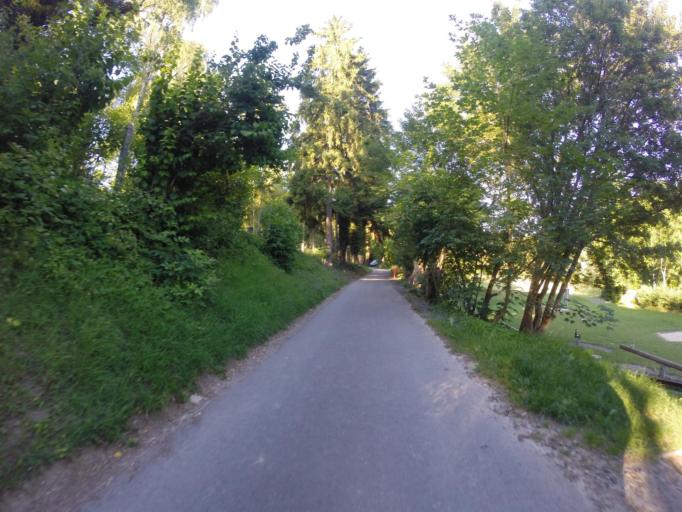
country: DE
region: Thuringia
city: Jena
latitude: 50.9193
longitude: 11.6283
